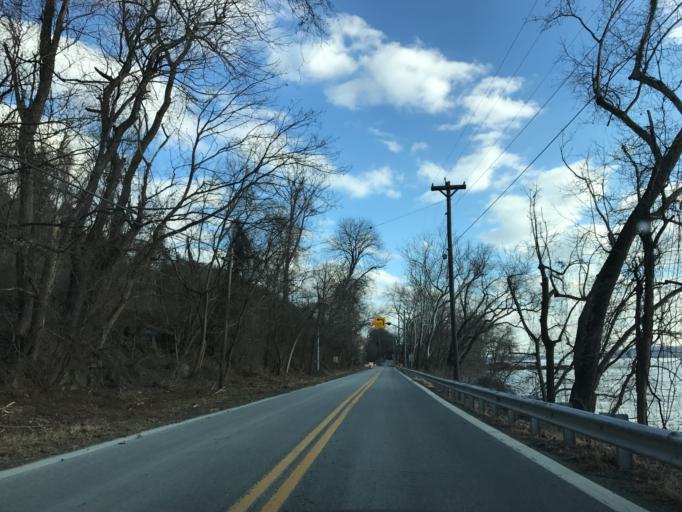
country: US
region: Maryland
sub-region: Harford County
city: Havre de Grace
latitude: 39.6156
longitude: -76.1290
